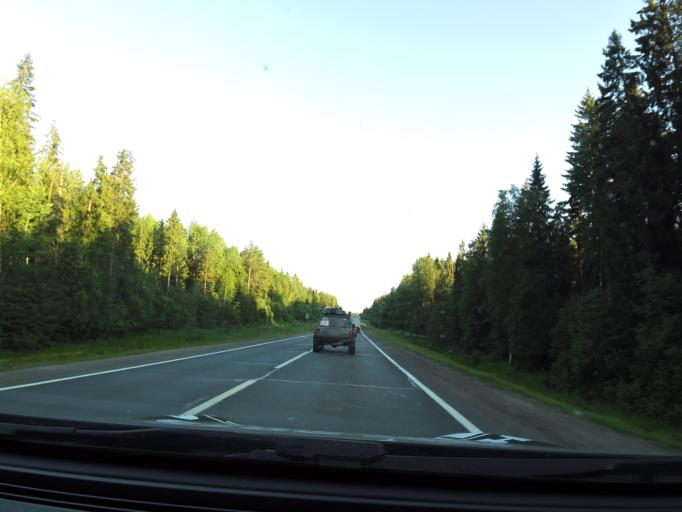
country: RU
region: Vologda
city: Gryazovets
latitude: 58.8677
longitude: 40.1974
